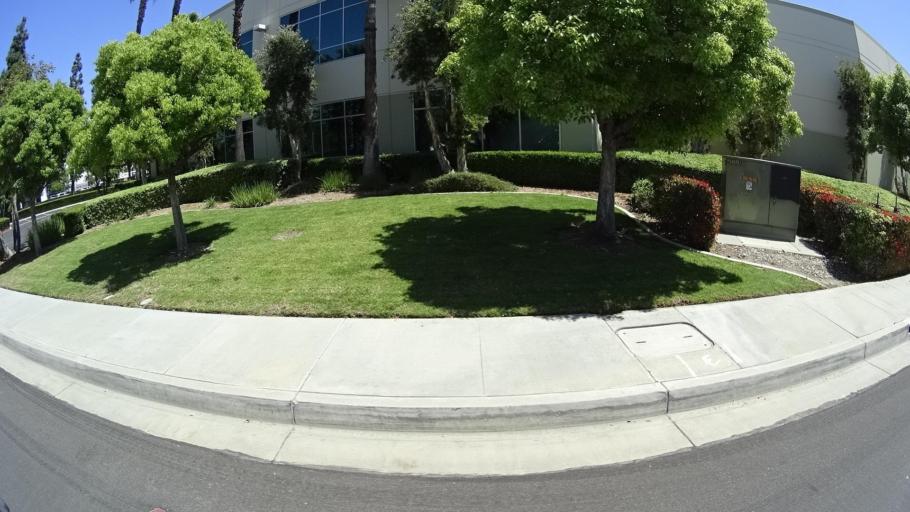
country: US
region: California
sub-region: Los Angeles County
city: La Puente
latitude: 34.0171
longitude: -117.9614
